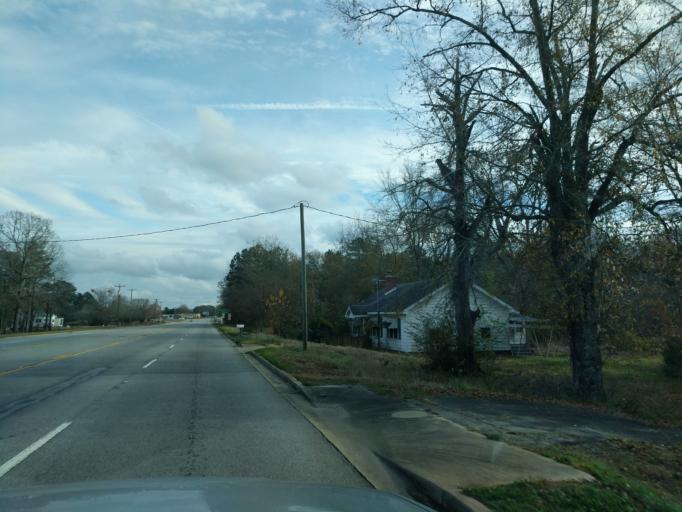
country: US
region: South Carolina
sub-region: Anderson County
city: Honea Path
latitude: 34.5040
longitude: -82.2941
